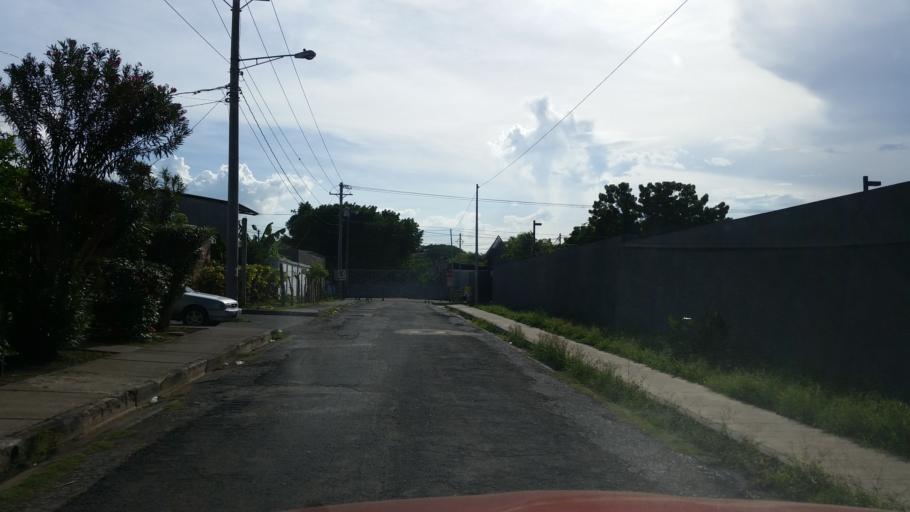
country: NI
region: Managua
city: Managua
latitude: 12.1528
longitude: -86.2690
